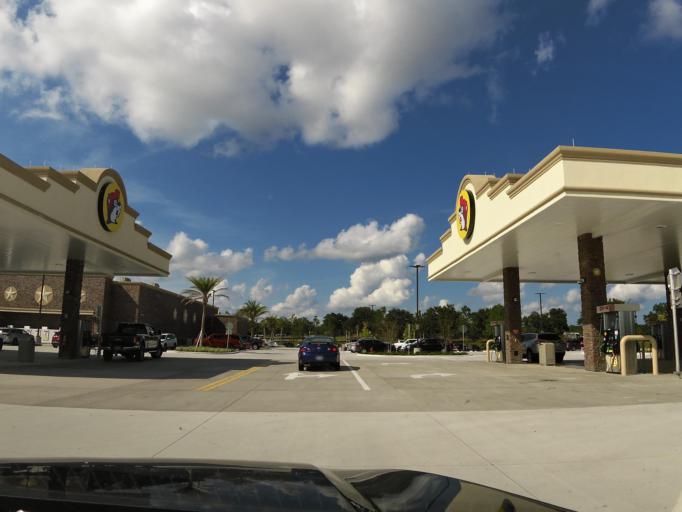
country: US
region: Florida
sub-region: Saint Johns County
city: Villano Beach
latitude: 29.9833
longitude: -81.4633
